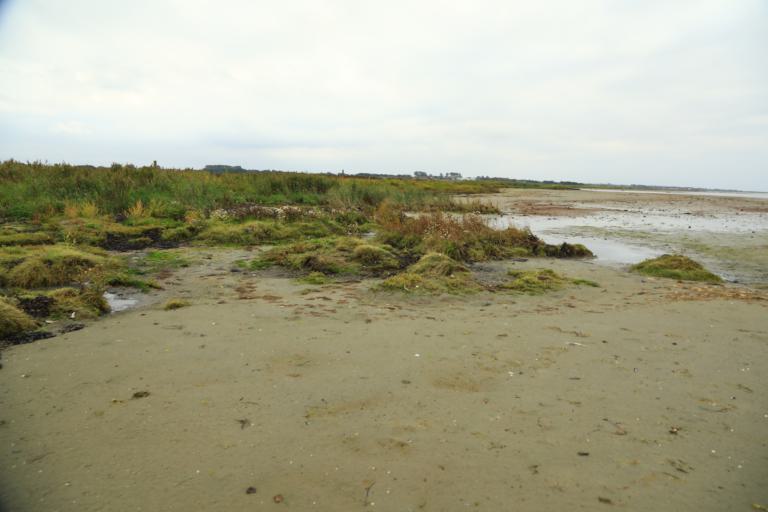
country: SE
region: Halland
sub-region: Varbergs Kommun
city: Tvaaker
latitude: 56.9953
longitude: 12.3548
